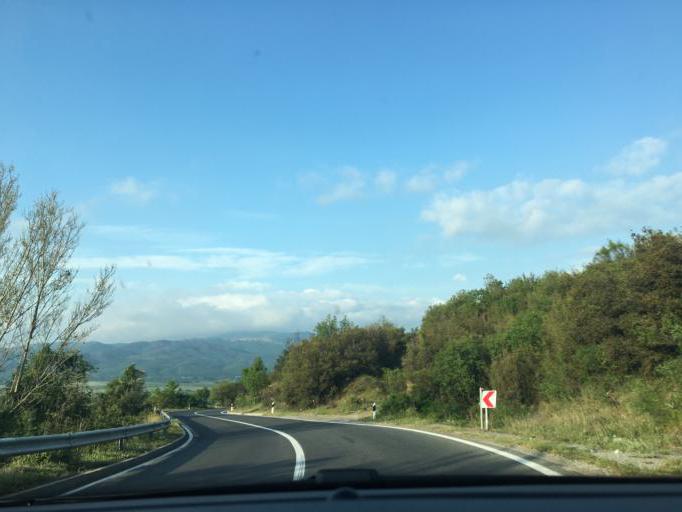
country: MK
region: Valandovo
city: Valandovo
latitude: 41.3215
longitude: 22.5984
